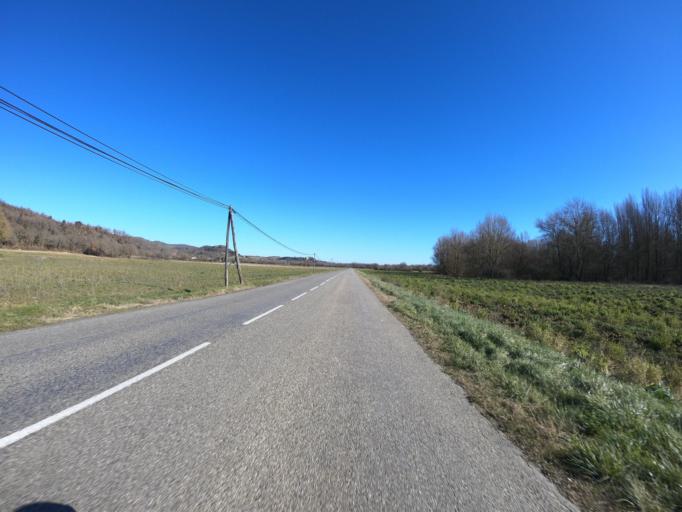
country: FR
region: Midi-Pyrenees
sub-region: Departement de l'Ariege
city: Mirepoix
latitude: 43.0947
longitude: 1.8497
